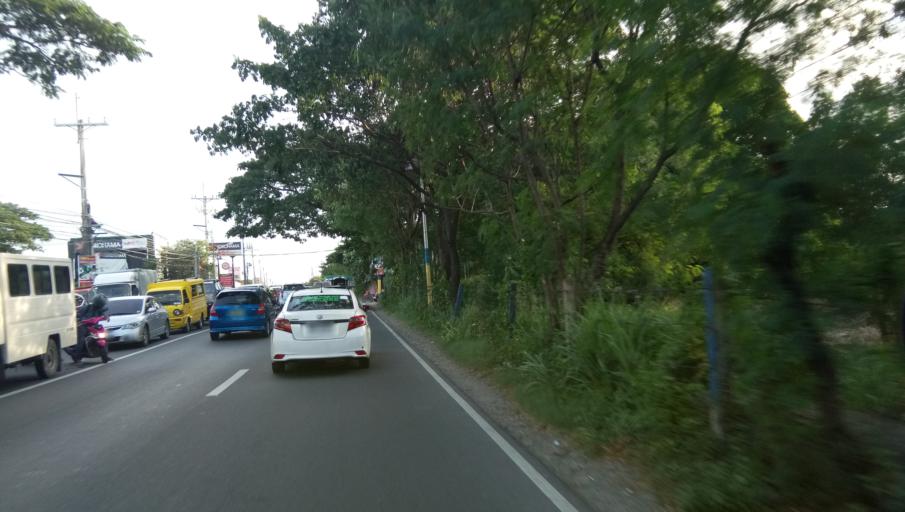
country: PH
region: Calabarzon
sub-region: Province of Cavite
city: Dasmarinas
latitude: 14.3773
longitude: 120.9792
